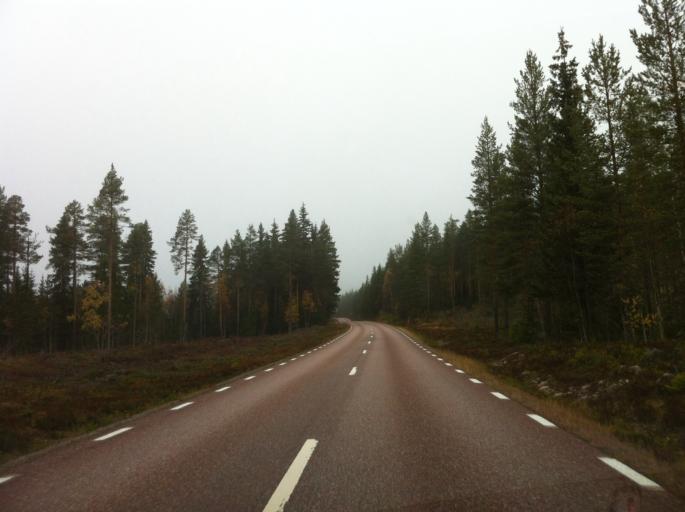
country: NO
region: Hedmark
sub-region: Trysil
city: Innbygda
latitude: 61.7792
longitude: 12.9416
